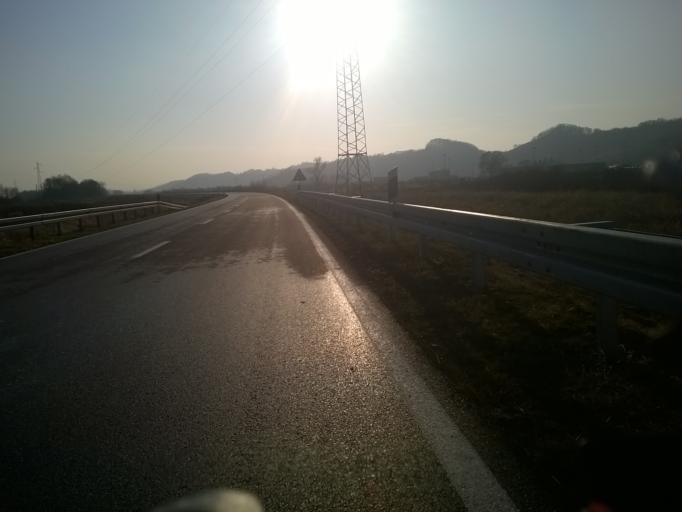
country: HR
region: Krapinsko-Zagorska
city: Zabok
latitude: 46.0703
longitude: 15.9143
